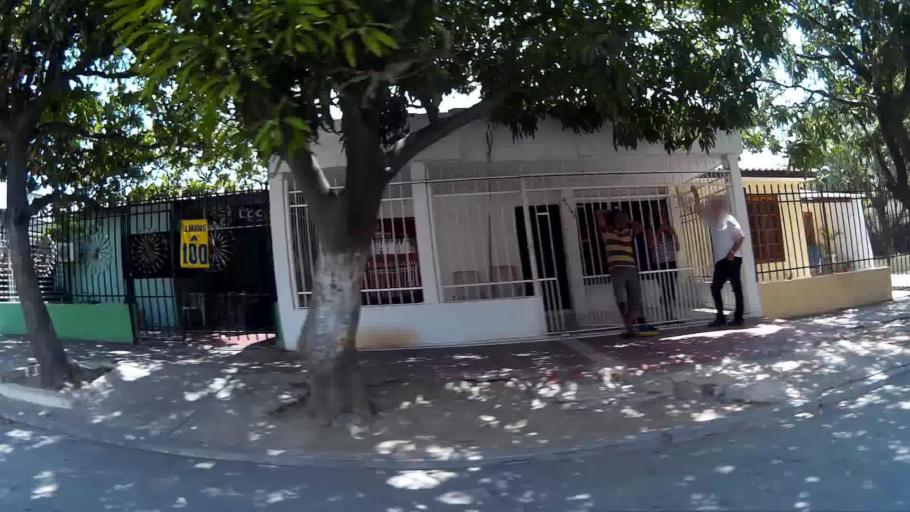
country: CO
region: Magdalena
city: Santa Marta
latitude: 11.2255
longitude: -74.2002
